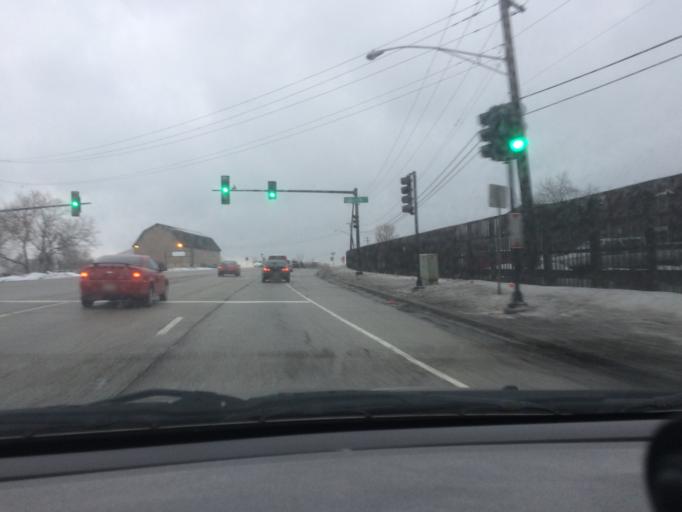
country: US
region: Illinois
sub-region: Cook County
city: Bartlett
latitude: 41.9949
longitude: -88.1654
